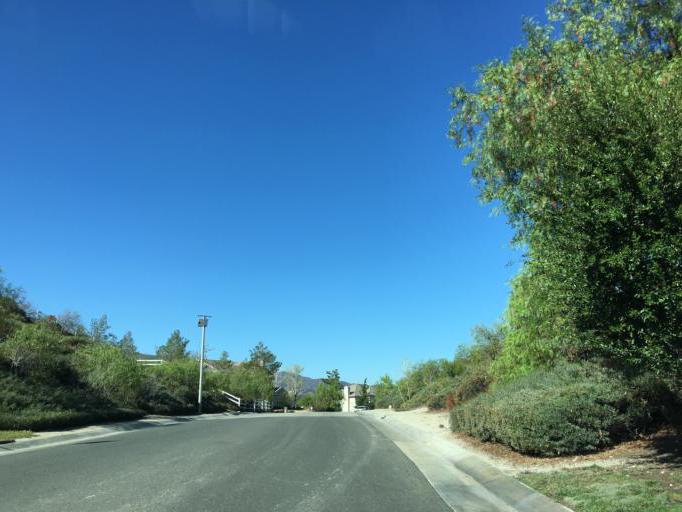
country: US
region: California
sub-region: Los Angeles County
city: Agua Dulce
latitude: 34.4039
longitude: -118.4009
